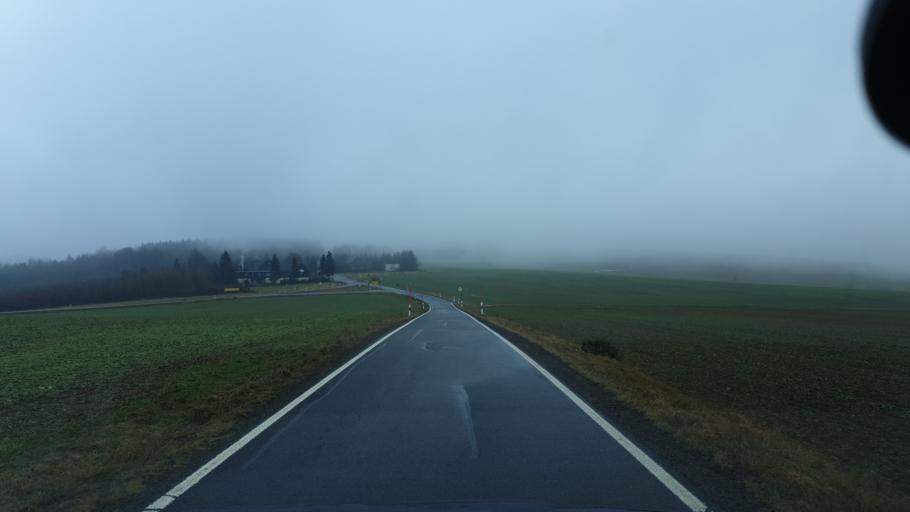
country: DE
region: Saxony
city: Neuhausen
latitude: 50.6582
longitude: 13.4734
